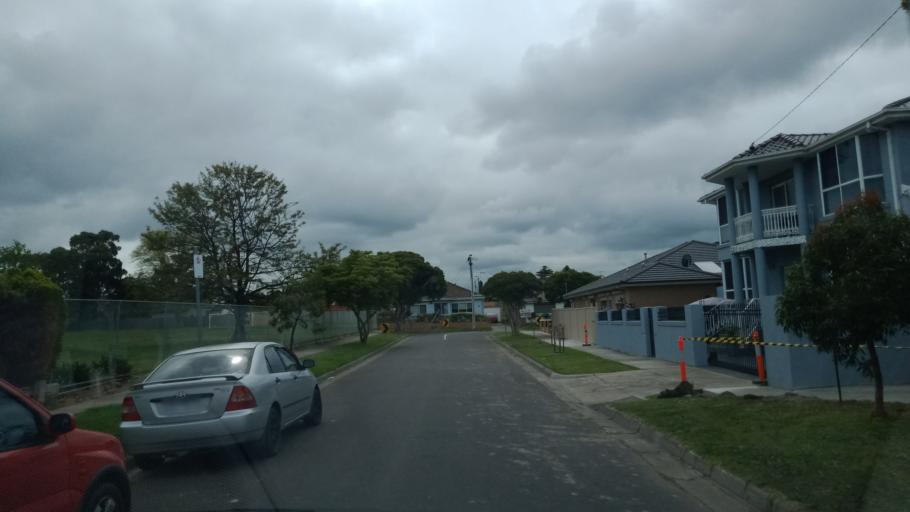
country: AU
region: Victoria
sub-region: Casey
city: Doveton
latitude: -37.9891
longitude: 145.2214
